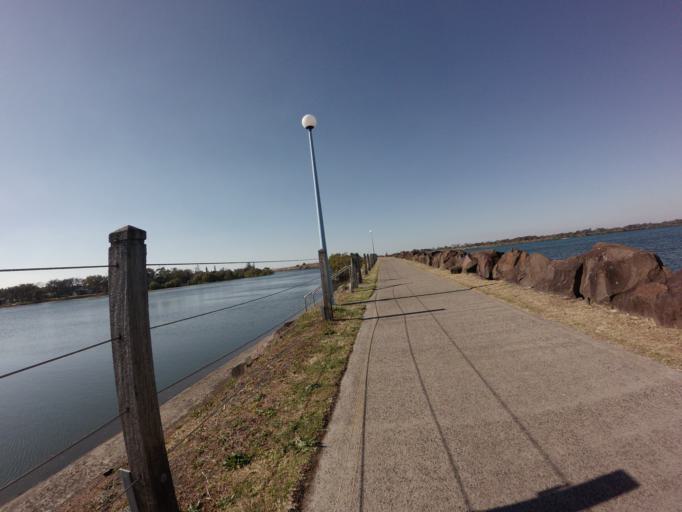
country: AU
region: New South Wales
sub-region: Ballina
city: East Ballina
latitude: -28.8688
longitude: 153.5816
